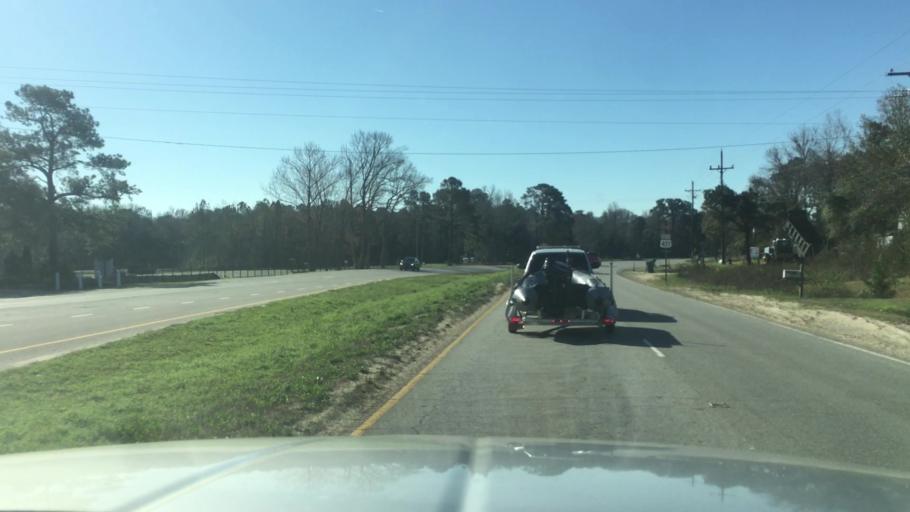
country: US
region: North Carolina
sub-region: New Hanover County
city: Sea Breeze
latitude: 34.0794
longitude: -77.8946
